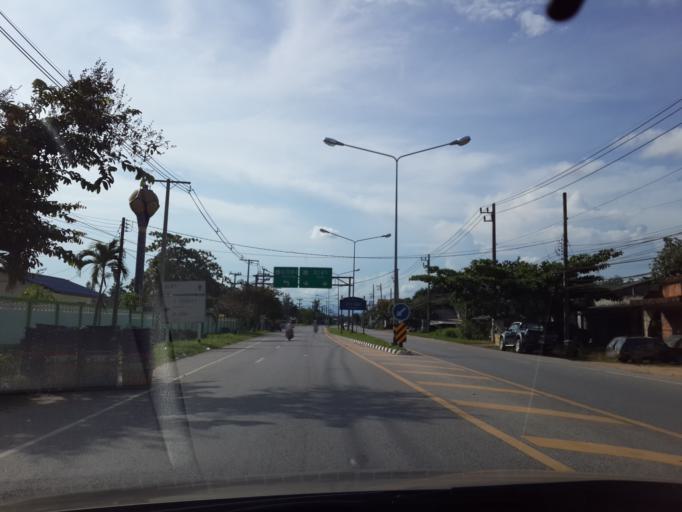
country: TH
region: Yala
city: Yala
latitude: 6.5010
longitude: 101.2893
